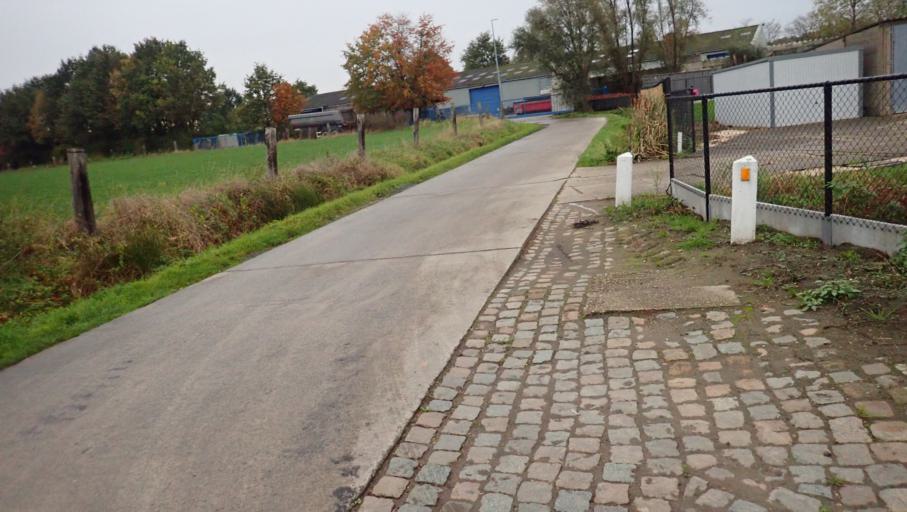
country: BE
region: Flanders
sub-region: Provincie Antwerpen
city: Berlaar
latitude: 51.1100
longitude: 4.6275
